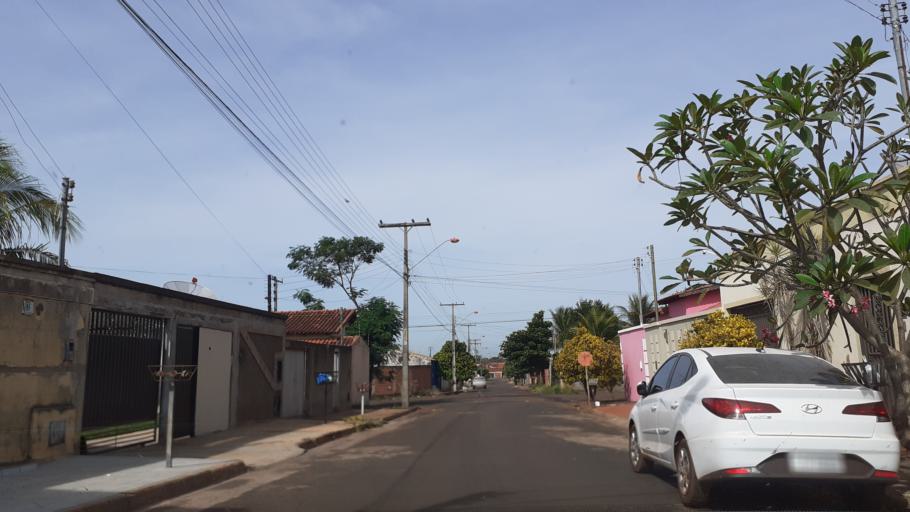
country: BR
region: Goias
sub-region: Itumbiara
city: Itumbiara
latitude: -18.4200
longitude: -49.2406
